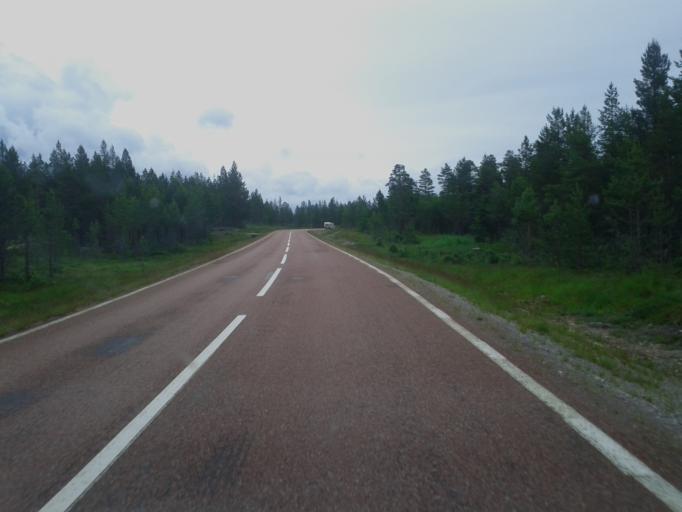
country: NO
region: Hedmark
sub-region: Engerdal
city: Engerdal
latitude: 61.8096
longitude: 12.3623
